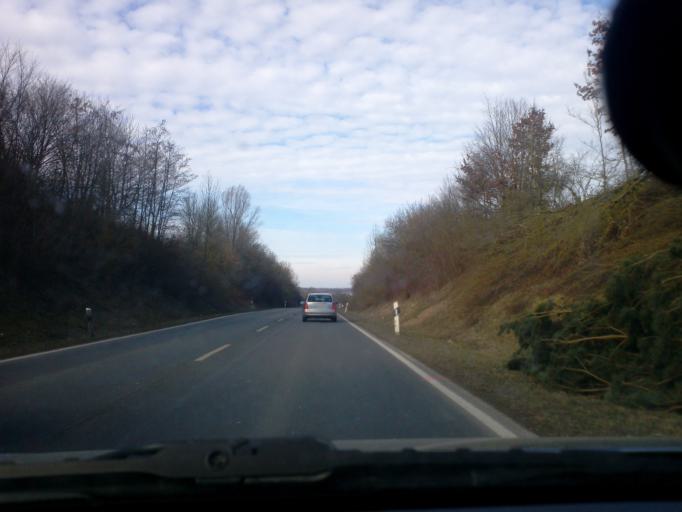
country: DE
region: Baden-Wuerttemberg
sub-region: Regierungsbezirk Stuttgart
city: Gemmingen
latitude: 49.1392
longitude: 8.9964
